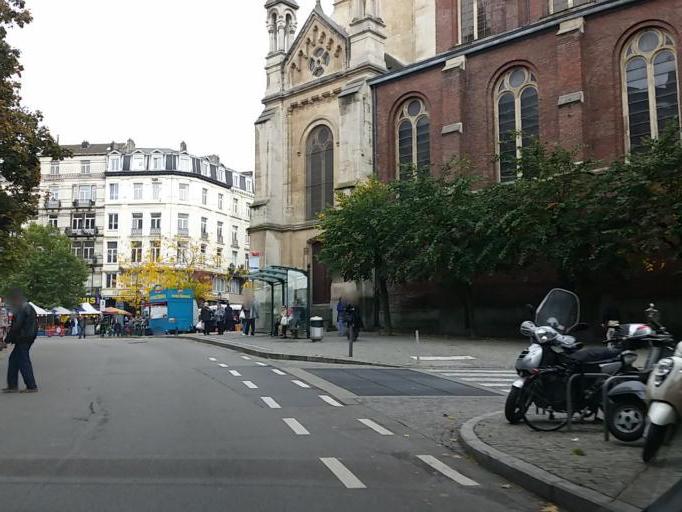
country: BE
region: Brussels Capital
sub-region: Bruxelles-Capitale
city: Brussels
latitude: 50.8311
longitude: 4.3439
